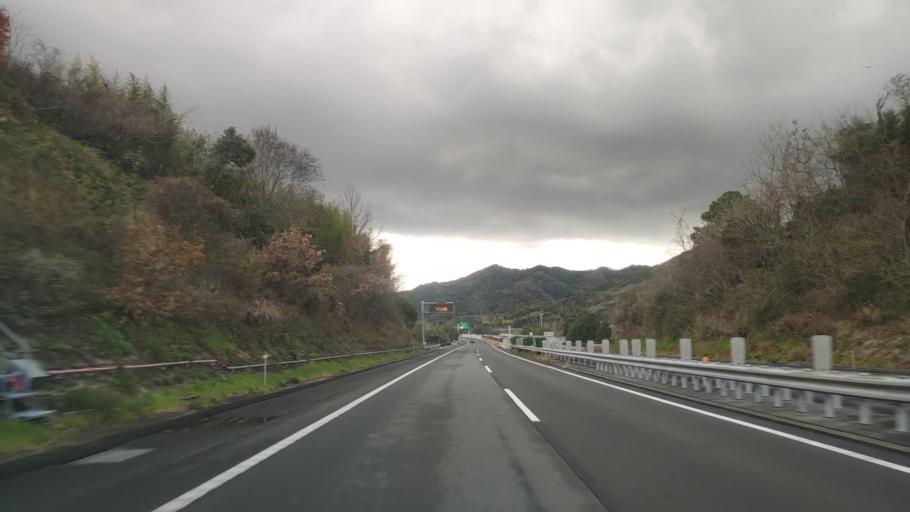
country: JP
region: Hyogo
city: Sumoto
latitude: 34.3454
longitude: 134.8492
